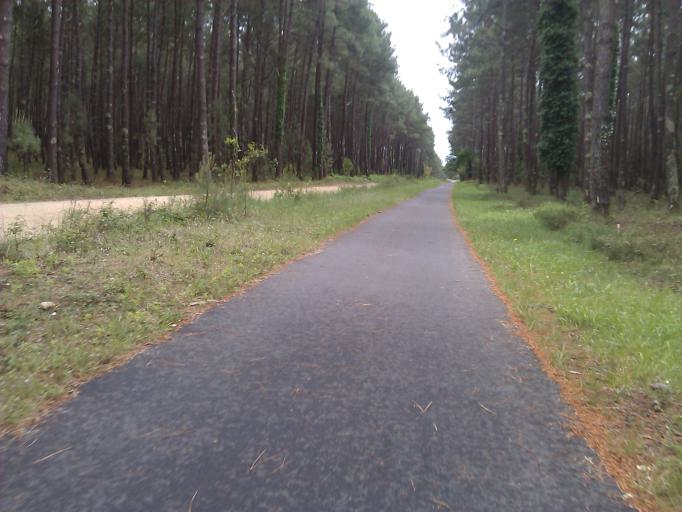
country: FR
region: Aquitaine
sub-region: Departement des Landes
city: Vielle-Saint-Girons
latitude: 43.9330
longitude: -1.3528
